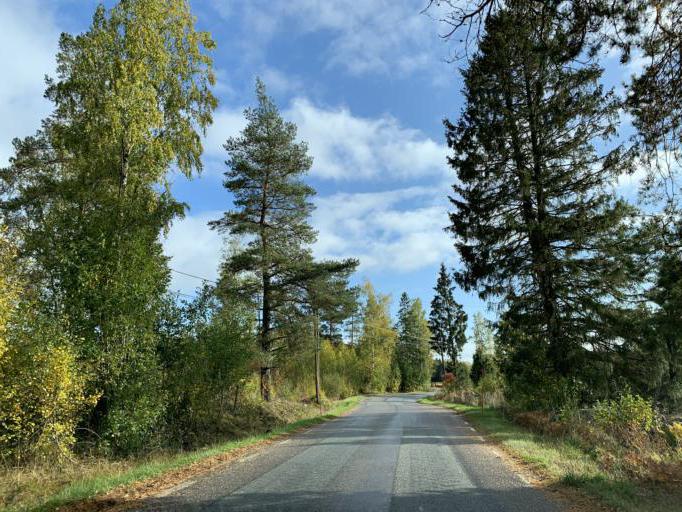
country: SE
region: Soedermanland
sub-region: Eskilstuna Kommun
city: Kvicksund
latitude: 59.3177
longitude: 16.2699
